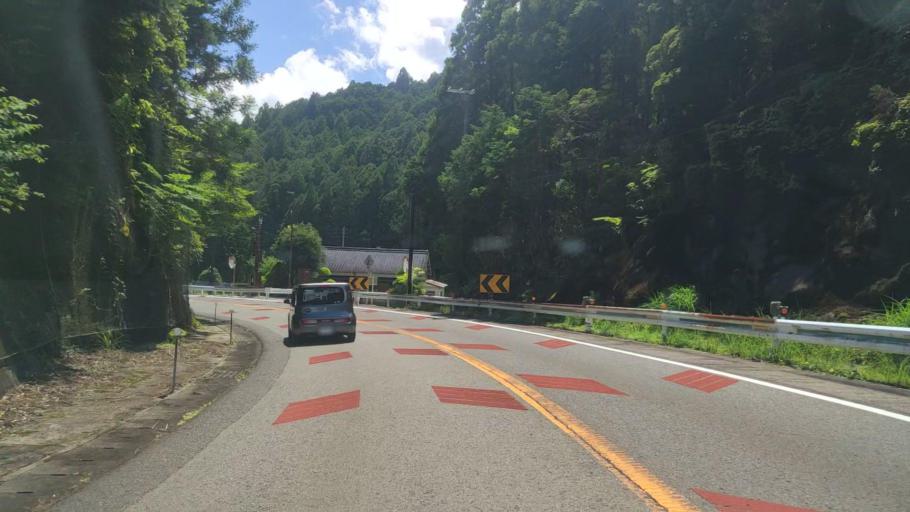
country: JP
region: Mie
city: Owase
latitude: 33.9867
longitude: 136.1082
